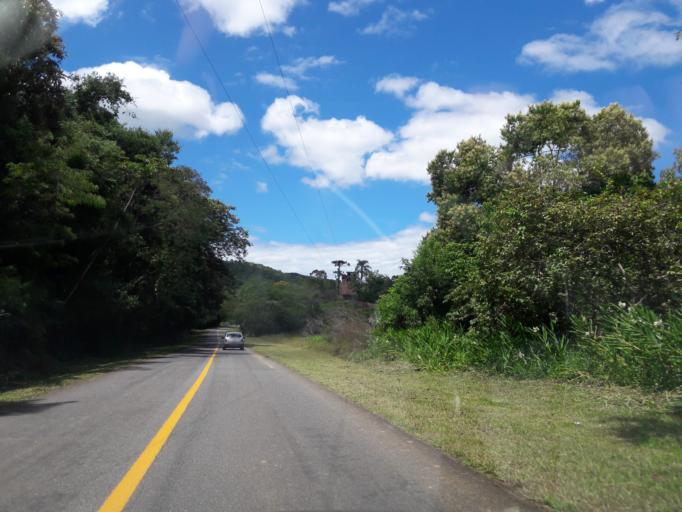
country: BR
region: Parana
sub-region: Antonina
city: Antonina
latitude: -25.4166
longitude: -48.8303
